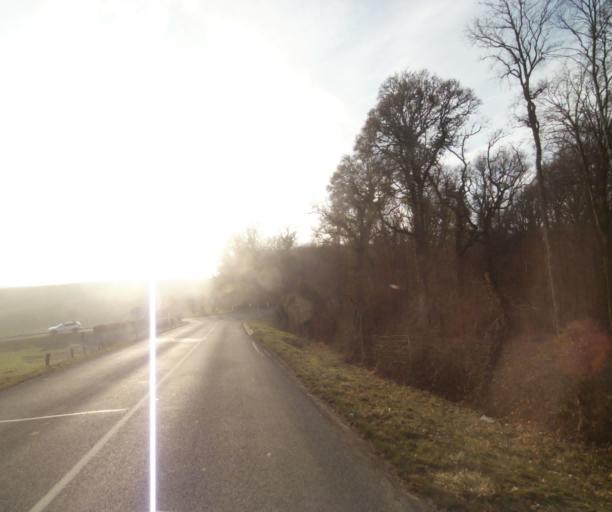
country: FR
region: Champagne-Ardenne
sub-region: Departement de la Haute-Marne
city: Chancenay
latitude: 48.7153
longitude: 4.9456
